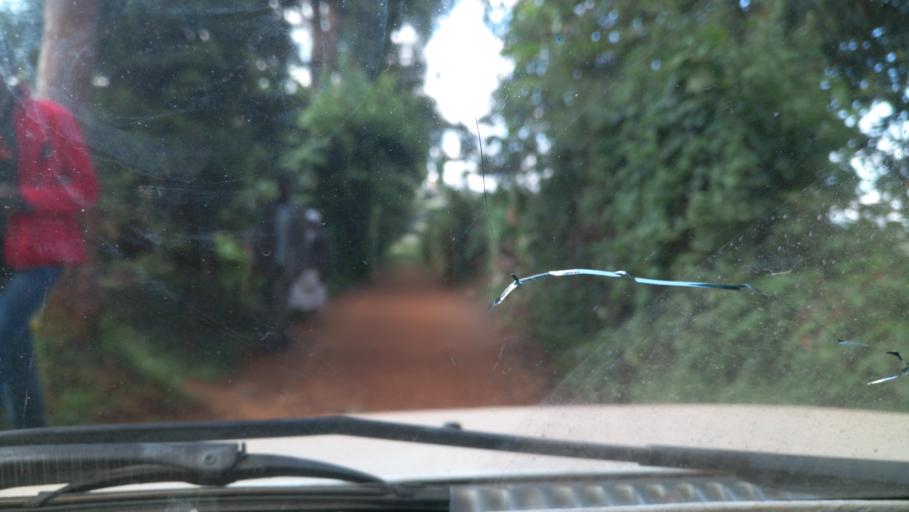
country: KE
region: Murang'a District
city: Kangema
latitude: -0.7968
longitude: 36.8676
